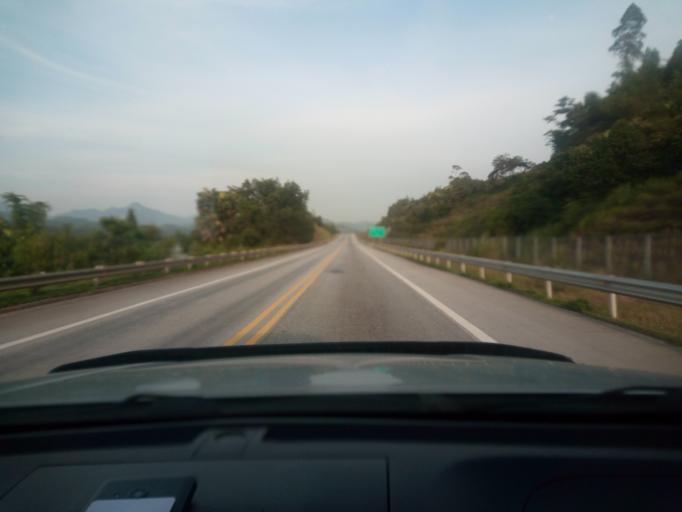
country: VN
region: Yen Bai
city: Co Phuc
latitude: 21.8871
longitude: 104.6575
